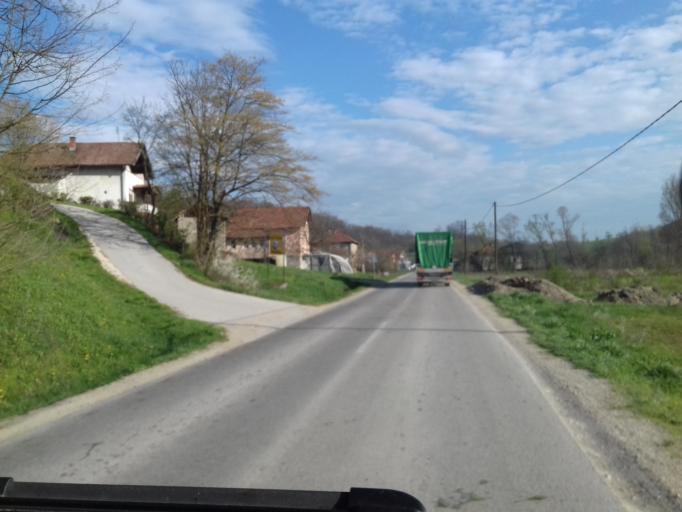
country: BA
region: Federation of Bosnia and Herzegovina
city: Tesanjka
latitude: 44.6540
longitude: 18.0166
